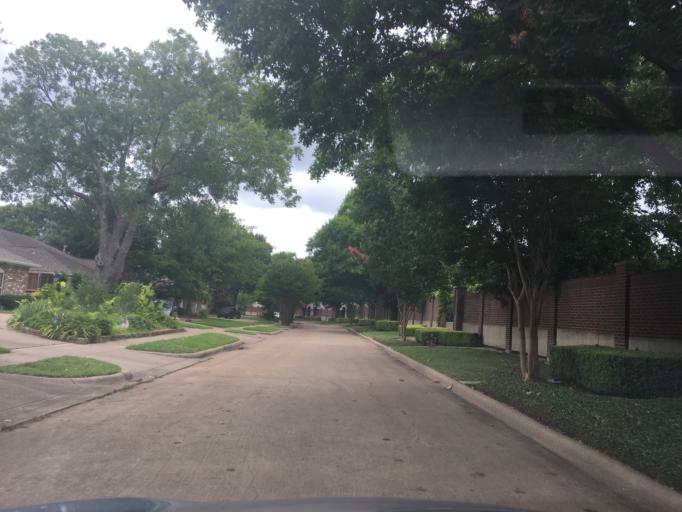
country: US
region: Texas
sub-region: Dallas County
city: Richardson
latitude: 32.9325
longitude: -96.7218
